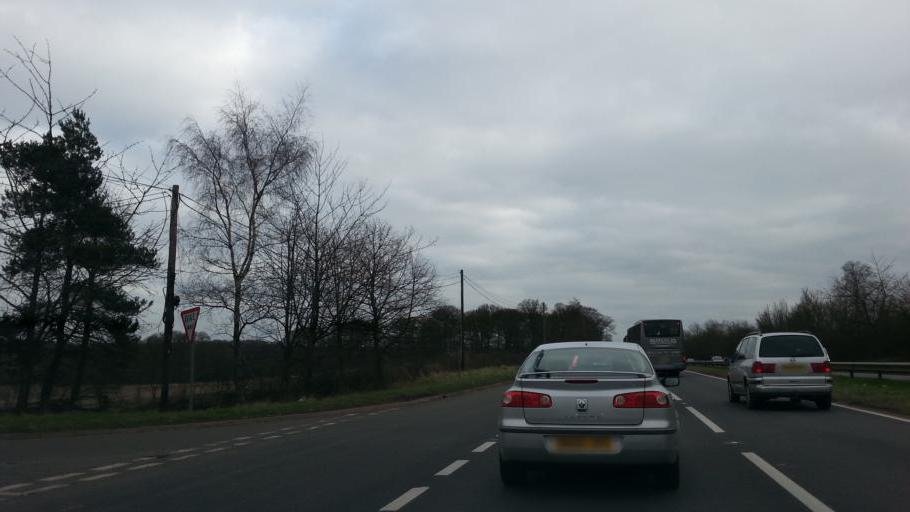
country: GB
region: England
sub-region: Solihull
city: Hampton in Arden
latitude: 52.4548
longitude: -1.6975
